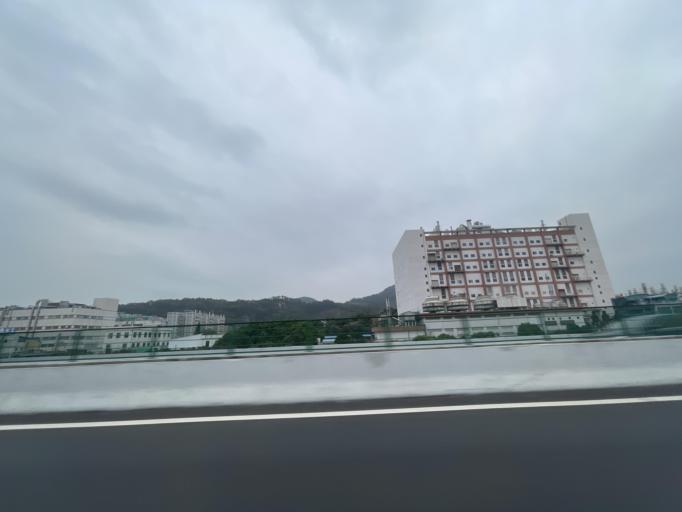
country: CN
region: Guangdong
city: Nansha
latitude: 22.7757
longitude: 113.5440
